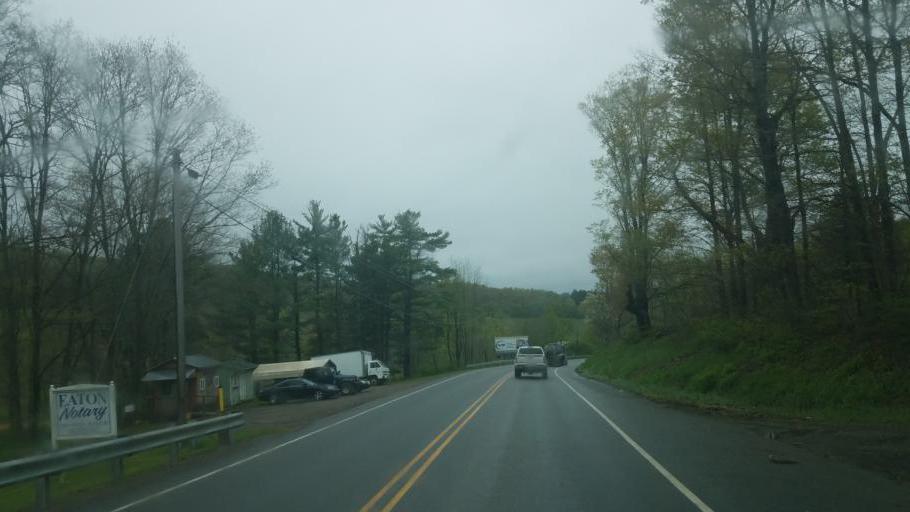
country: US
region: Pennsylvania
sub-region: McKean County
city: Smethport
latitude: 41.8149
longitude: -78.4044
